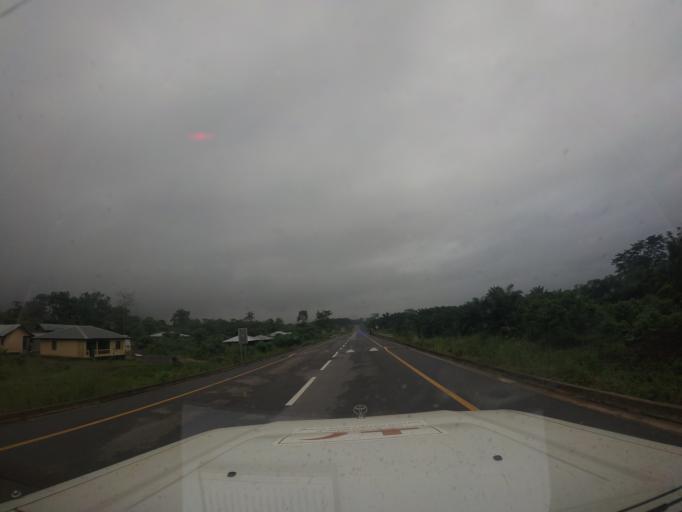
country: SL
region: Eastern Province
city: Hangha
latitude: 7.9609
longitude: -11.1358
